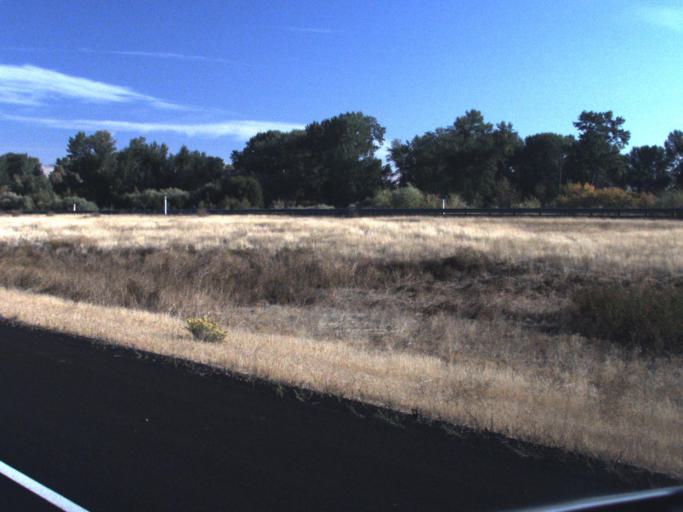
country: US
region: Washington
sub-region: Yakima County
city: Union Gap
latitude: 46.5438
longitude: -120.4705
